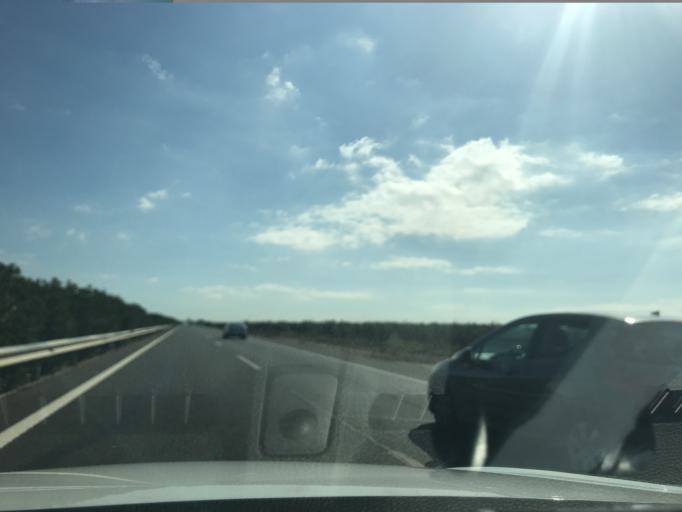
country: ES
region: Andalusia
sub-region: Provincia de Sevilla
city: Ecija
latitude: 37.5228
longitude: -5.1468
